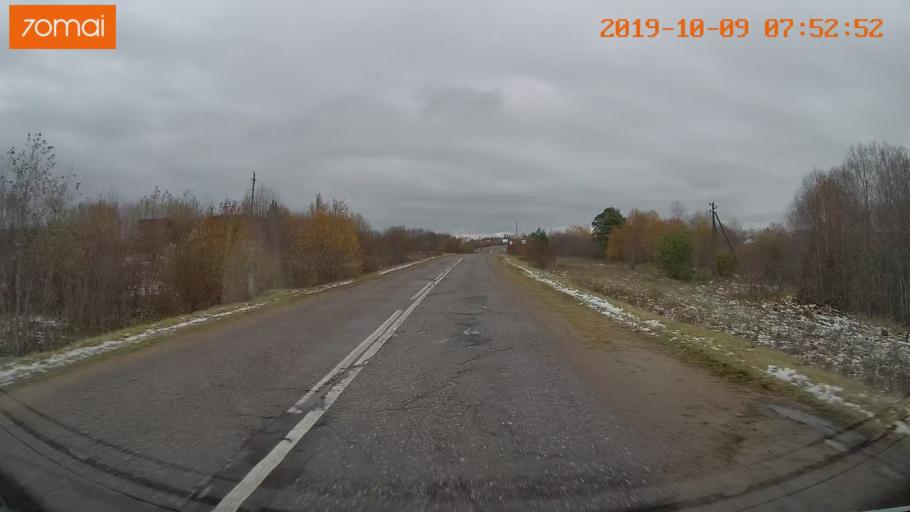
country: RU
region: Jaroslavl
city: Kukoboy
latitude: 58.6945
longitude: 39.8905
